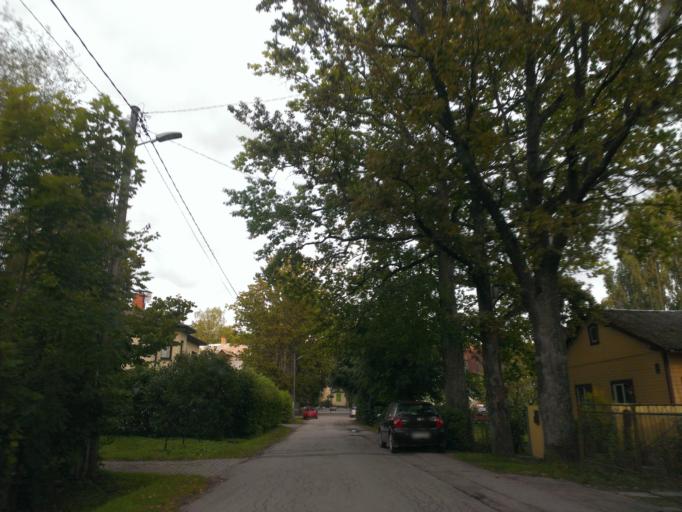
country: LV
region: Ogre
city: Ogre
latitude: 56.8187
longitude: 24.6042
